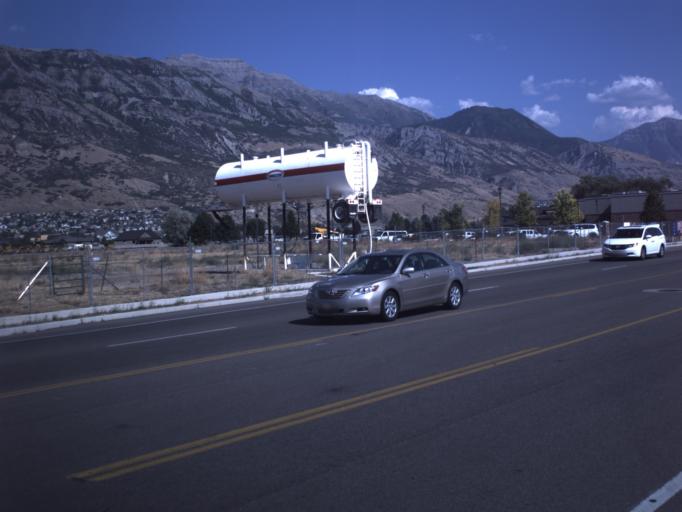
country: US
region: Utah
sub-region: Utah County
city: Cedar Hills
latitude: 40.3942
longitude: -111.7706
